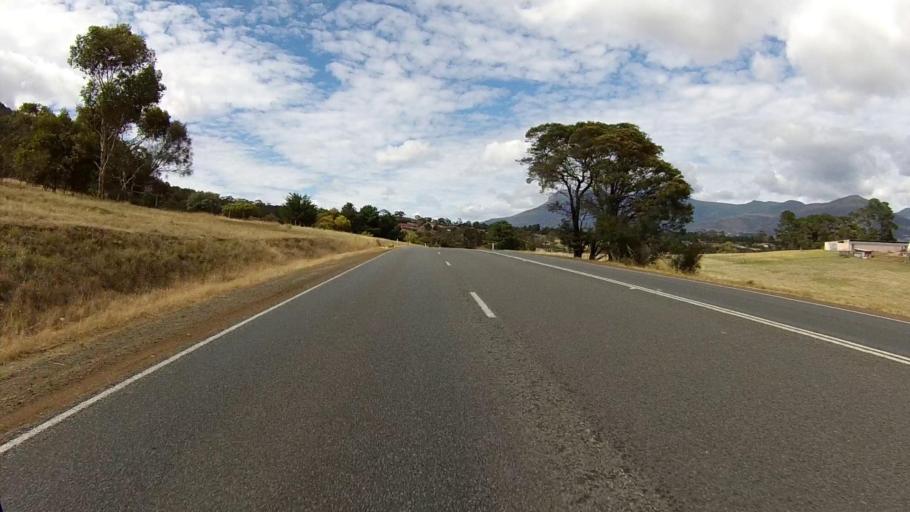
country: AU
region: Tasmania
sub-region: Brighton
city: Old Beach
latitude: -42.7924
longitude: 147.2931
